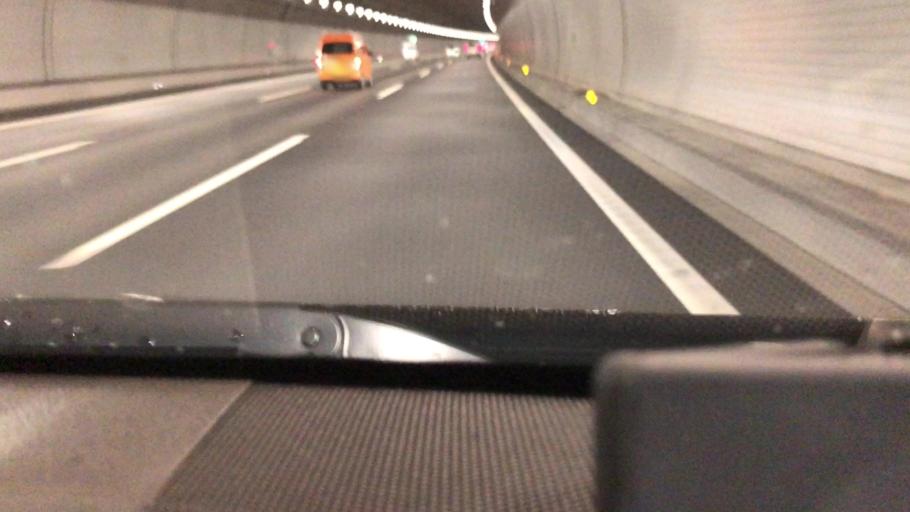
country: JP
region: Shizuoka
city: Kanaya
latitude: 34.8432
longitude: 138.0662
